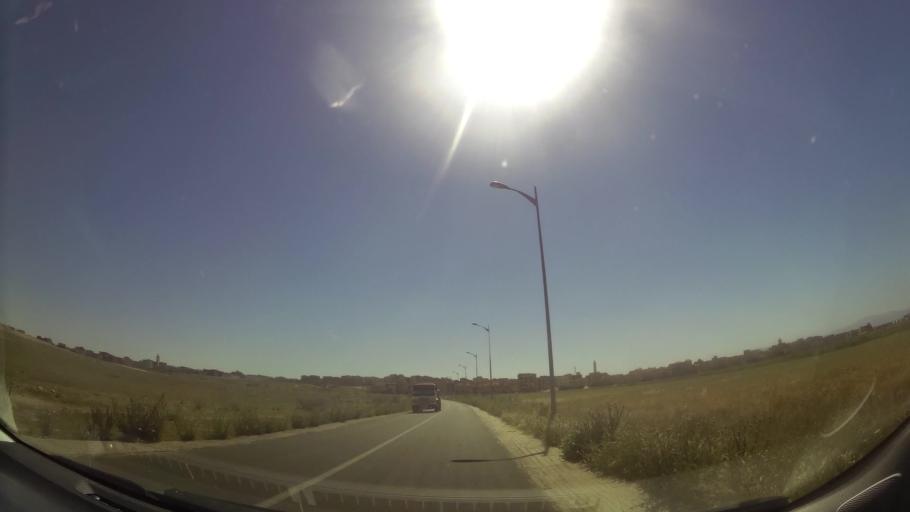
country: MA
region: Oriental
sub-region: Oujda-Angad
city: Oujda
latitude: 34.6929
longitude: -1.8652
